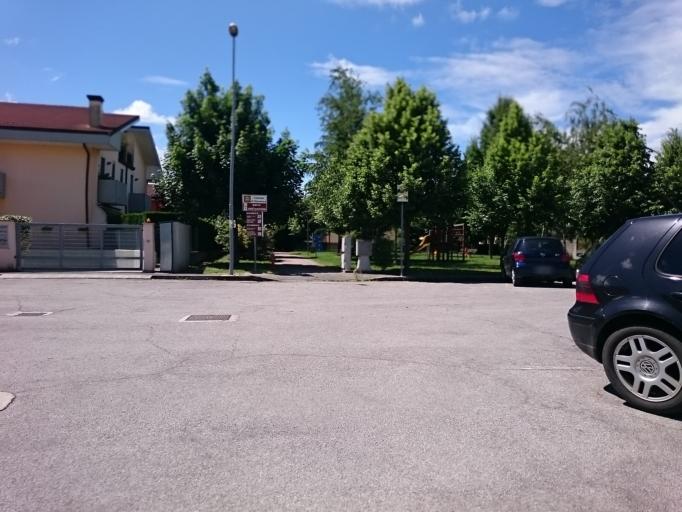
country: IT
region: Veneto
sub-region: Provincia di Padova
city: Polverara
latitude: 45.3082
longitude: 11.9544
